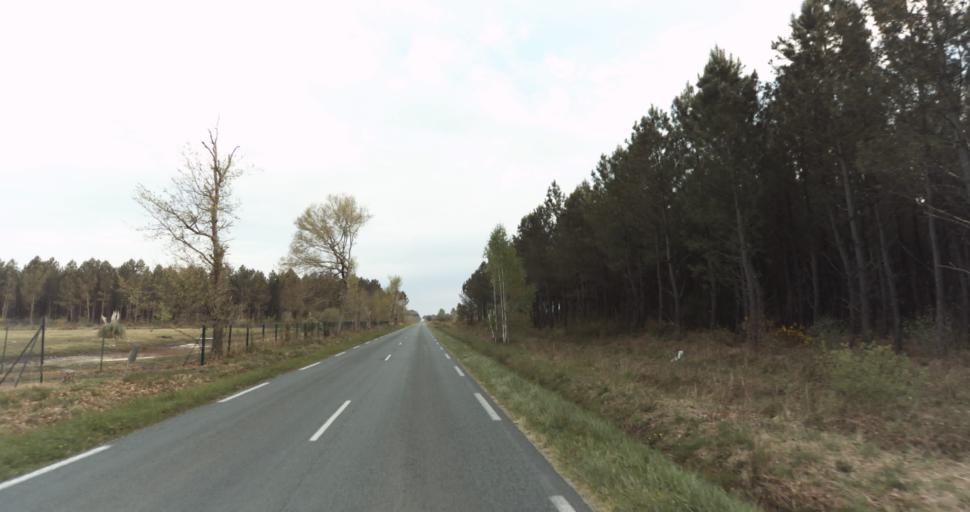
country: FR
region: Aquitaine
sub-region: Departement de la Gironde
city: Martignas-sur-Jalle
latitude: 44.7883
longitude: -0.7753
